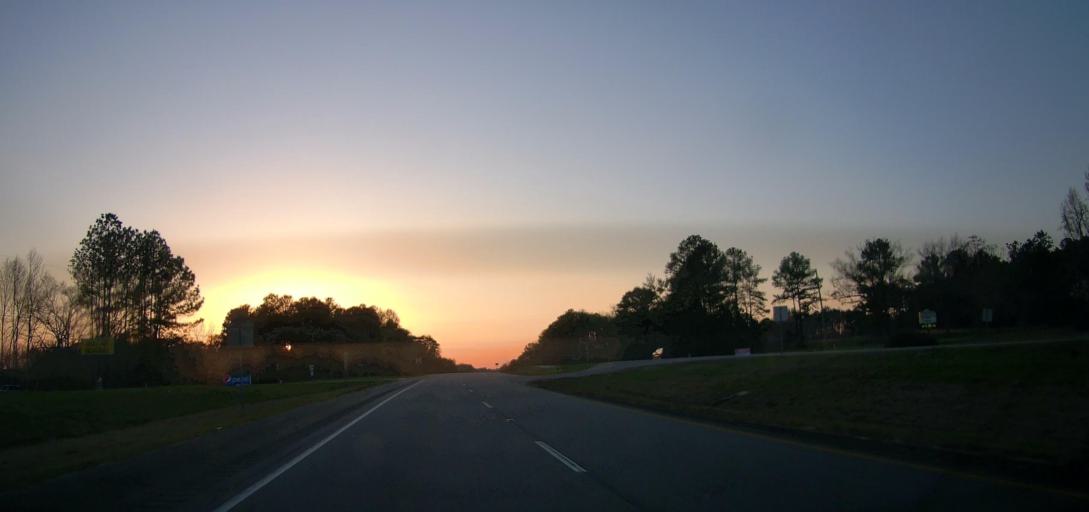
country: US
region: Alabama
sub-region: Tallapoosa County
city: Alexander City
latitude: 32.9754
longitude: -86.0385
